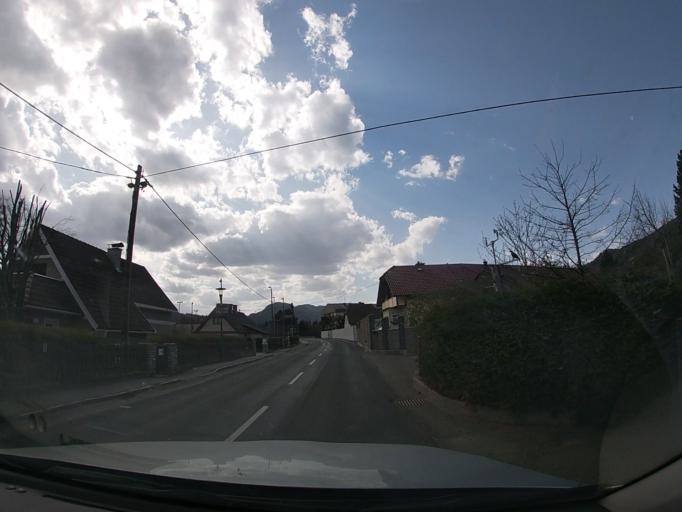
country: AT
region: Styria
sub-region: Politischer Bezirk Murtal
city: Poels
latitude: 47.2236
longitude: 14.5909
